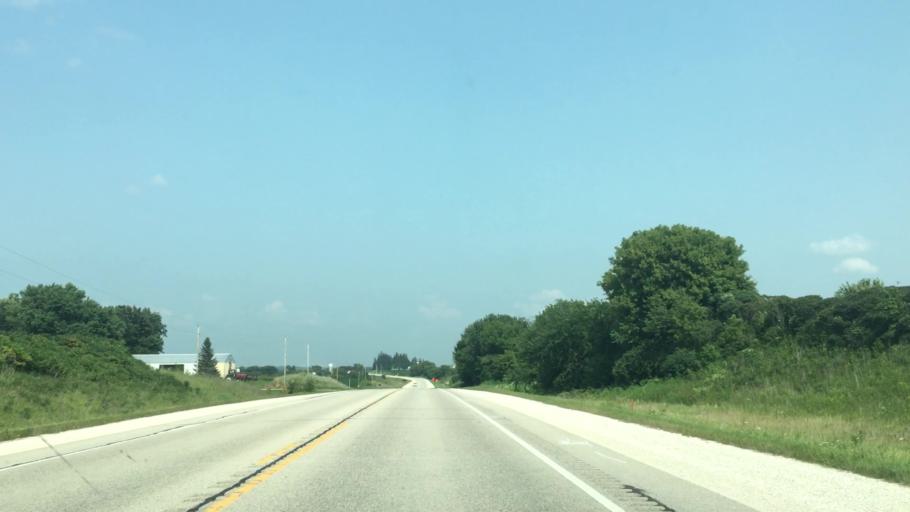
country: US
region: Iowa
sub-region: Winneshiek County
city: Decorah
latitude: 43.2736
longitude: -91.8243
